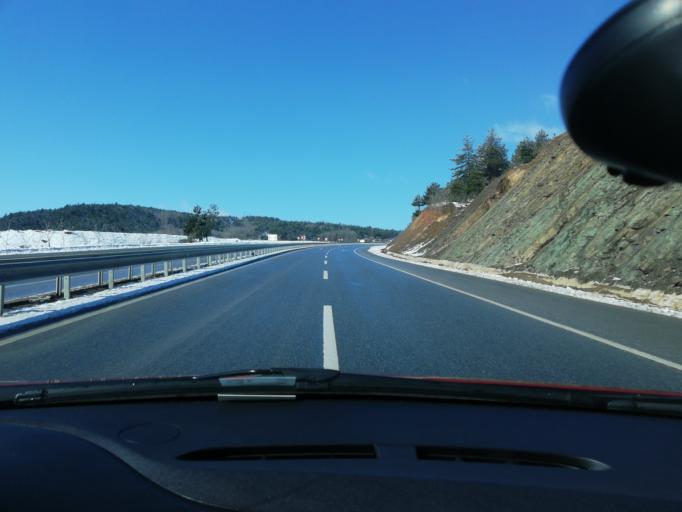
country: TR
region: Kastamonu
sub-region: Cide
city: Kastamonu
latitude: 41.3600
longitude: 33.6923
